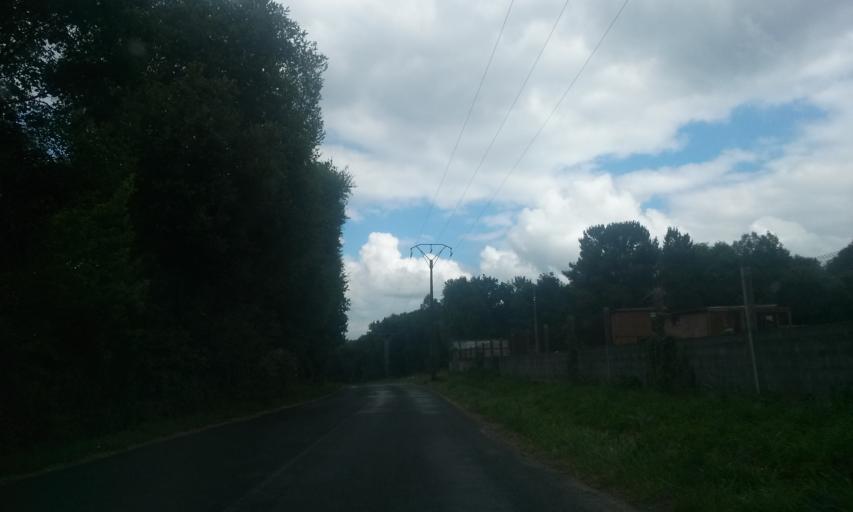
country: ES
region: Galicia
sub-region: Provincia de Lugo
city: Outeiro de Rei
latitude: 43.0609
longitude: -7.6095
